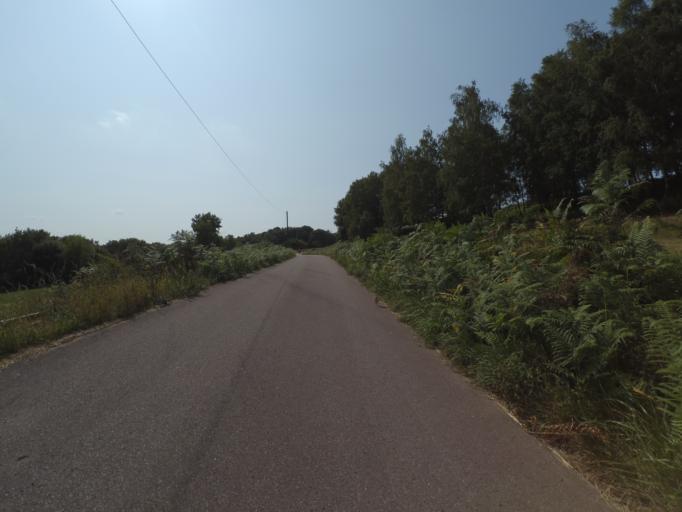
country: DE
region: Rheinland-Pfalz
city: Taben-Rodt
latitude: 49.5386
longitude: 6.5873
